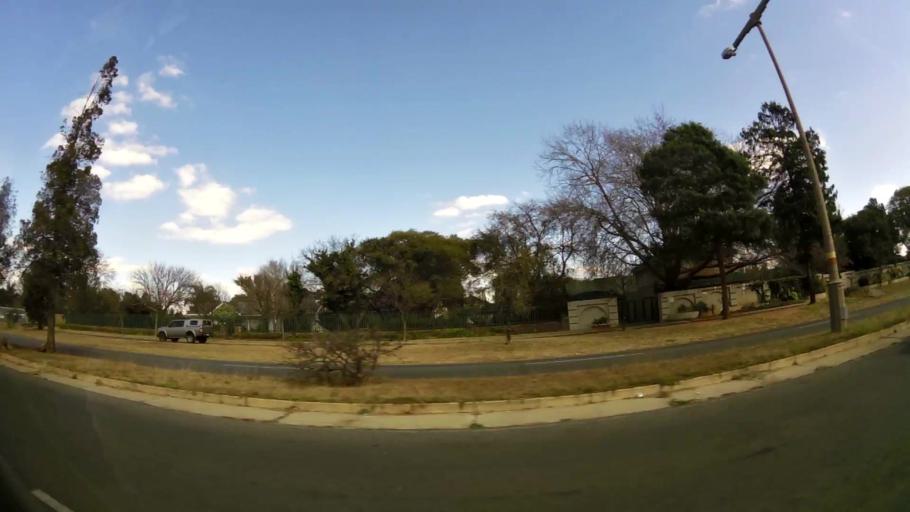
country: ZA
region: Gauteng
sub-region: West Rand District Municipality
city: Krugersdorp
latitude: -26.0973
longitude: 27.7936
